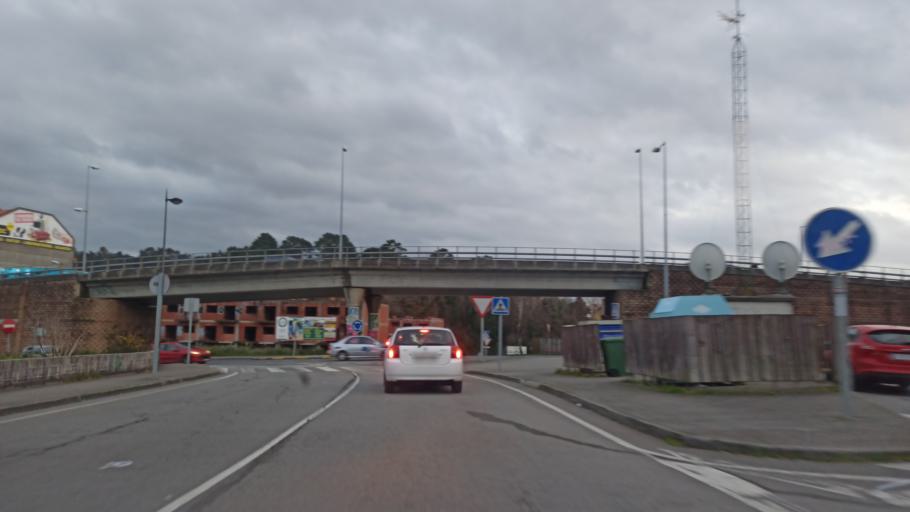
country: ES
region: Galicia
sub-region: Provincia da Coruna
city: Cambre
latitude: 43.3223
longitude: -8.3509
